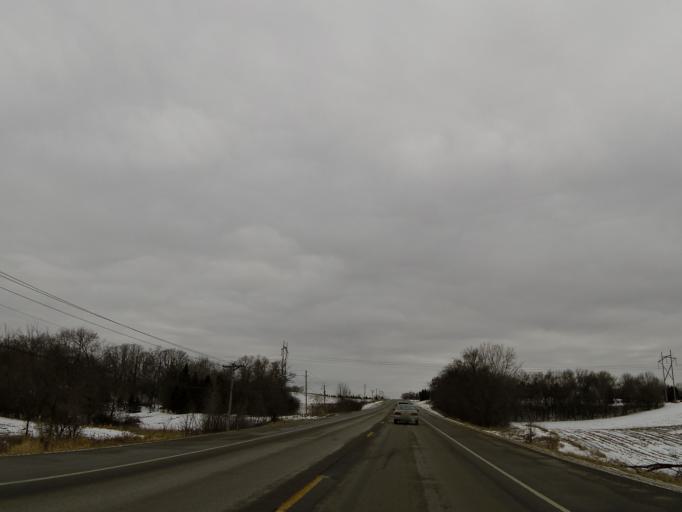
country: US
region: Minnesota
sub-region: Washington County
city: Cottage Grove
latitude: 44.8578
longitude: -92.9033
